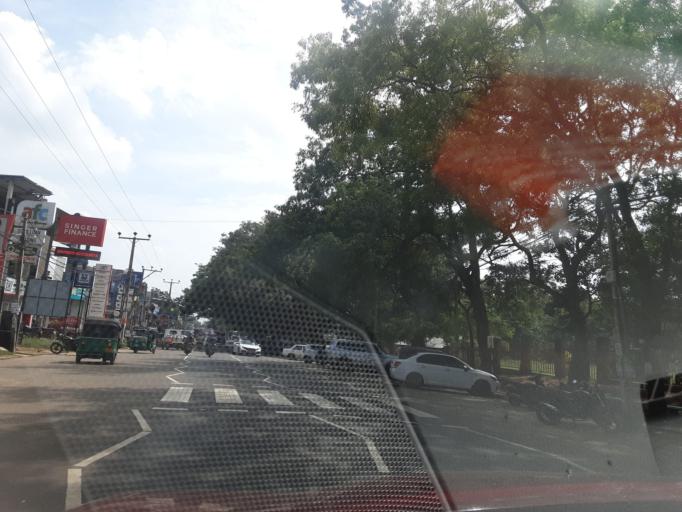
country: LK
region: Northern Province
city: Vavuniya
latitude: 8.5414
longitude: 80.4918
